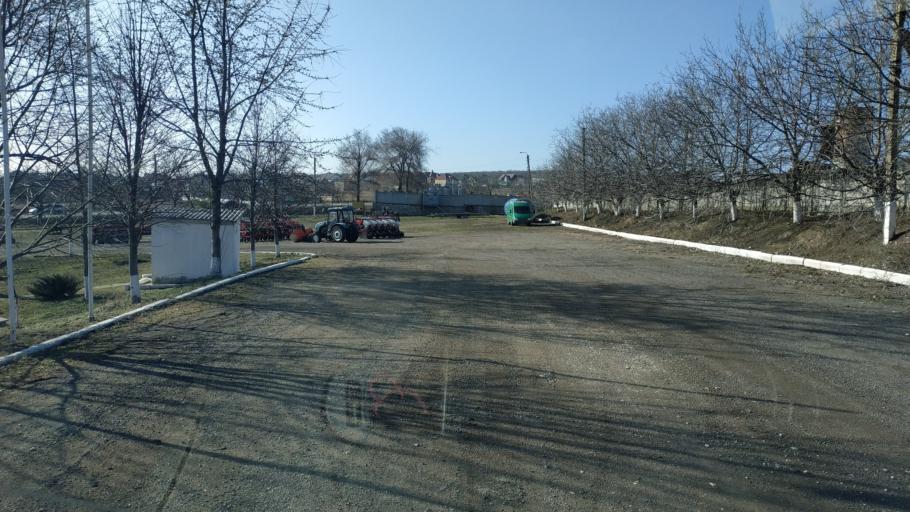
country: MD
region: Laloveni
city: Ialoveni
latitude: 46.9493
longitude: 28.7173
